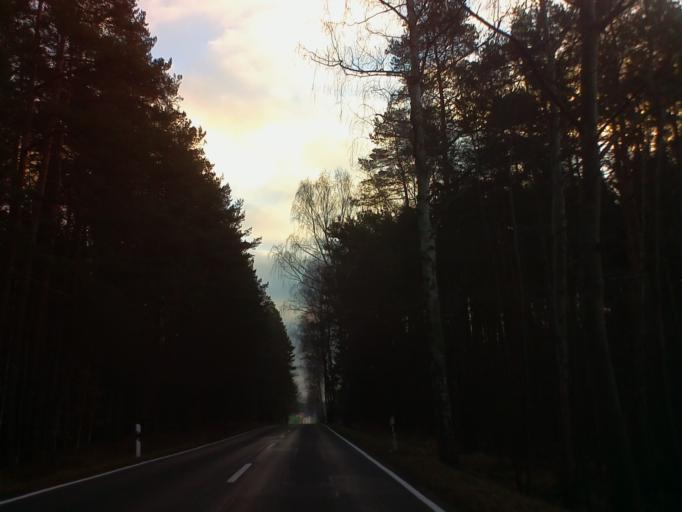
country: DE
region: Thuringia
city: Trockenborn-Wolfersdorf
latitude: 50.7613
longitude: 11.6824
